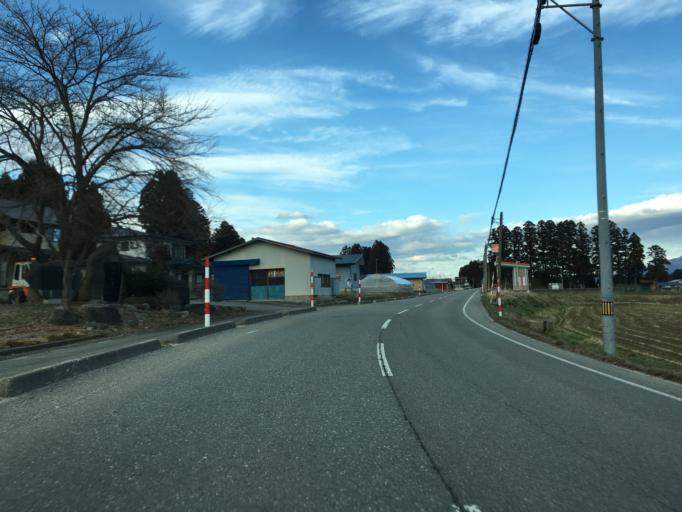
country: JP
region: Yamagata
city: Nagai
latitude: 38.1267
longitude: 140.0057
